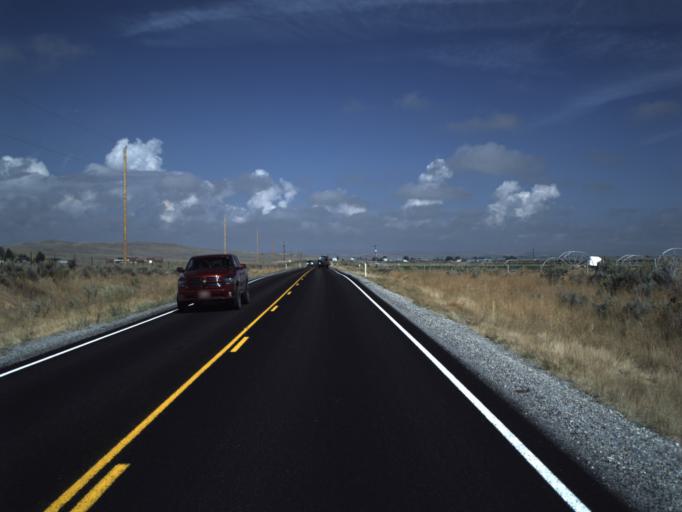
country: US
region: Utah
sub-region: Rich County
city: Randolph
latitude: 41.5801
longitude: -111.1653
